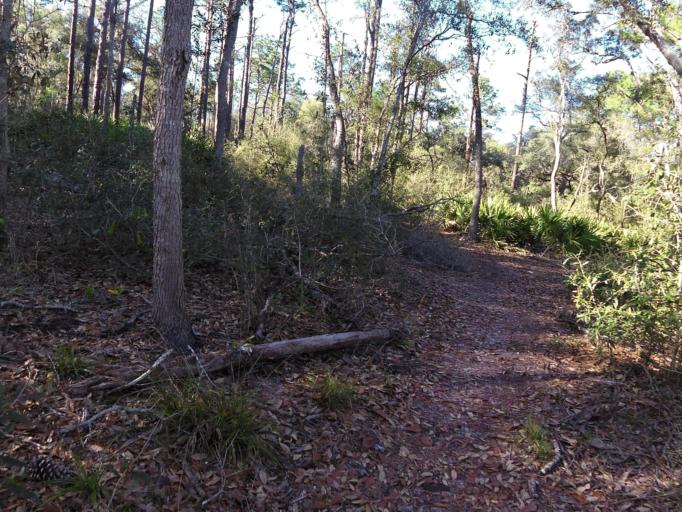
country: US
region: Florida
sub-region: Clay County
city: Keystone Heights
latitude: 29.8232
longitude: -82.0237
